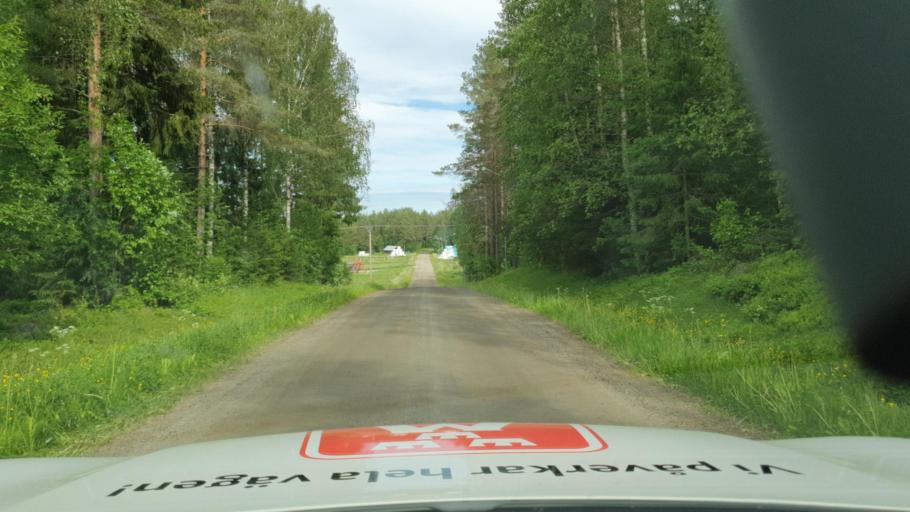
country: SE
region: Vaesterbotten
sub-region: Robertsfors Kommun
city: Robertsfors
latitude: 64.3733
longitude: 21.0570
